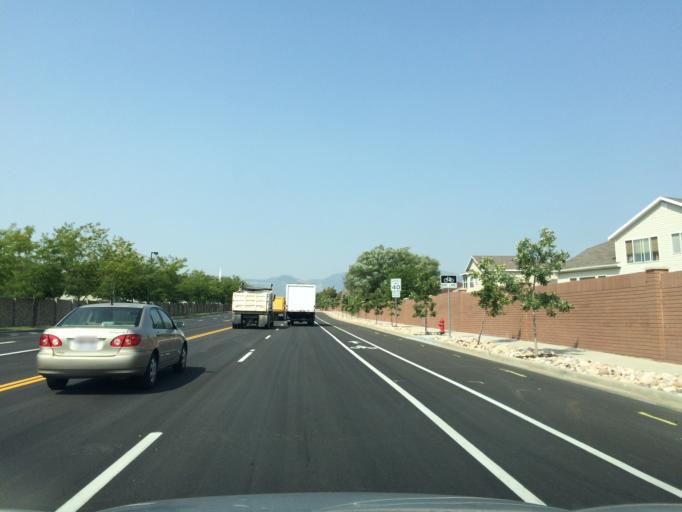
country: US
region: Utah
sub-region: Salt Lake County
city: Oquirrh
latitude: 40.5879
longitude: -112.0147
